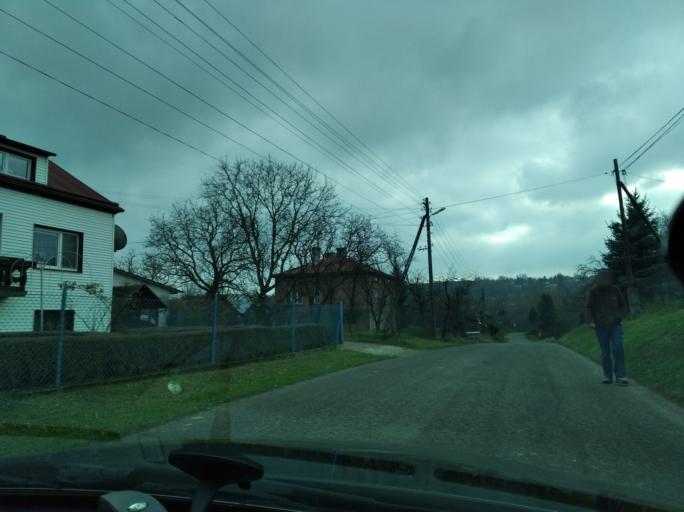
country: PL
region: Subcarpathian Voivodeship
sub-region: Powiat przeworski
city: Sietesz
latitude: 49.9831
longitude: 22.3451
